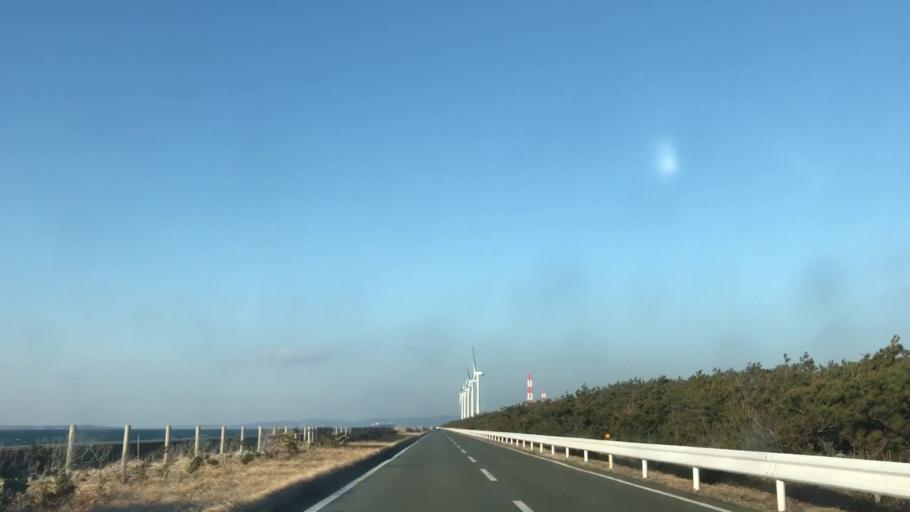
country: JP
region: Aichi
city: Toyohama
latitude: 34.6284
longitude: 137.0470
